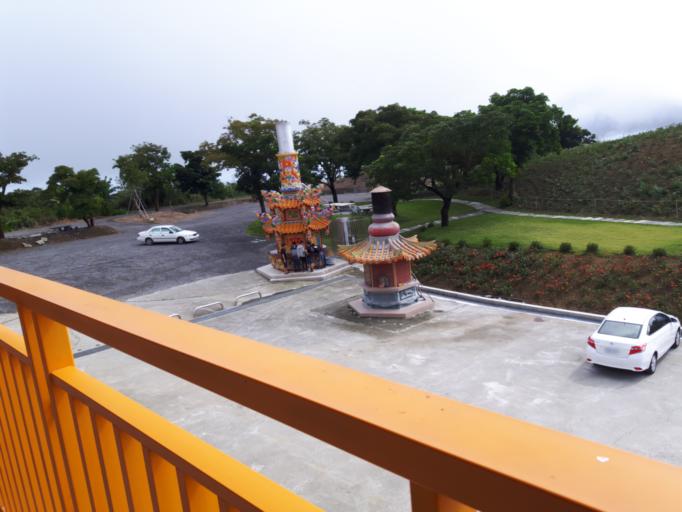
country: TW
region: Taiwan
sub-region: Hualien
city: Hualian
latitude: 23.8781
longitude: 121.5797
